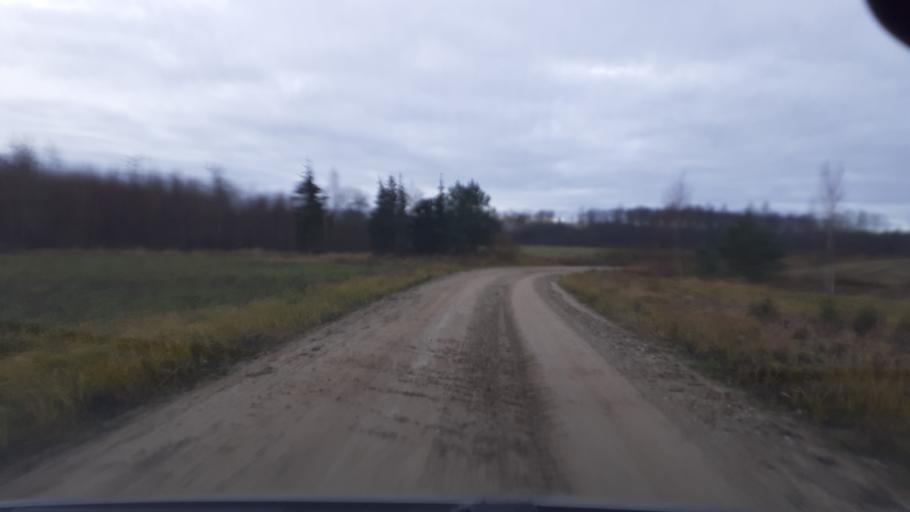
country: LV
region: Kuldigas Rajons
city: Kuldiga
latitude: 57.0056
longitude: 21.9283
